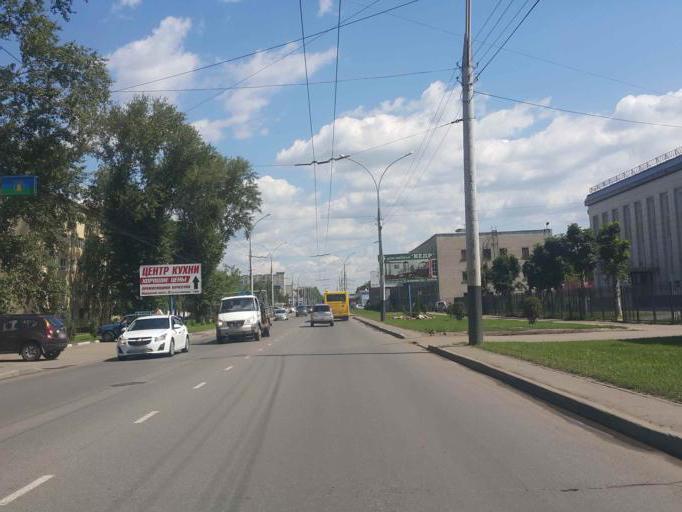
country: RU
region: Tambov
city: Tambov
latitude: 52.7456
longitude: 41.4550
